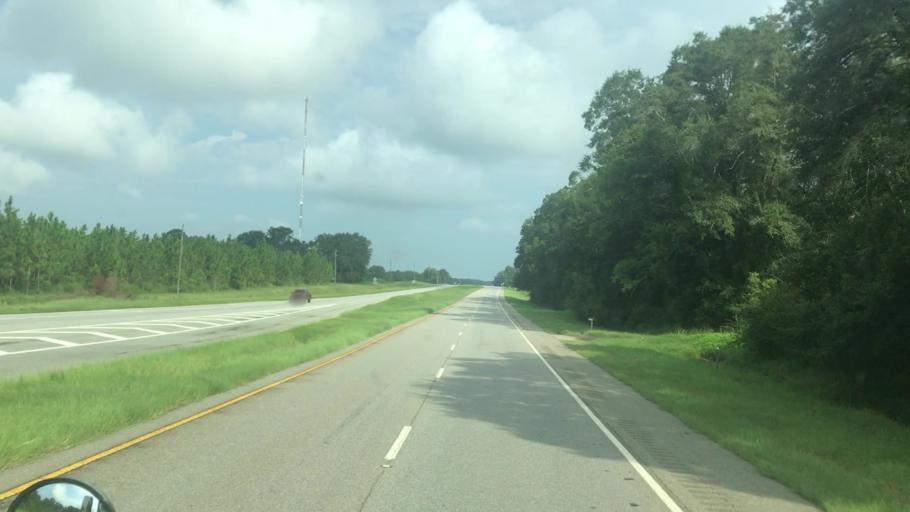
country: US
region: Georgia
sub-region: Miller County
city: Colquitt
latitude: 31.2612
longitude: -84.8131
